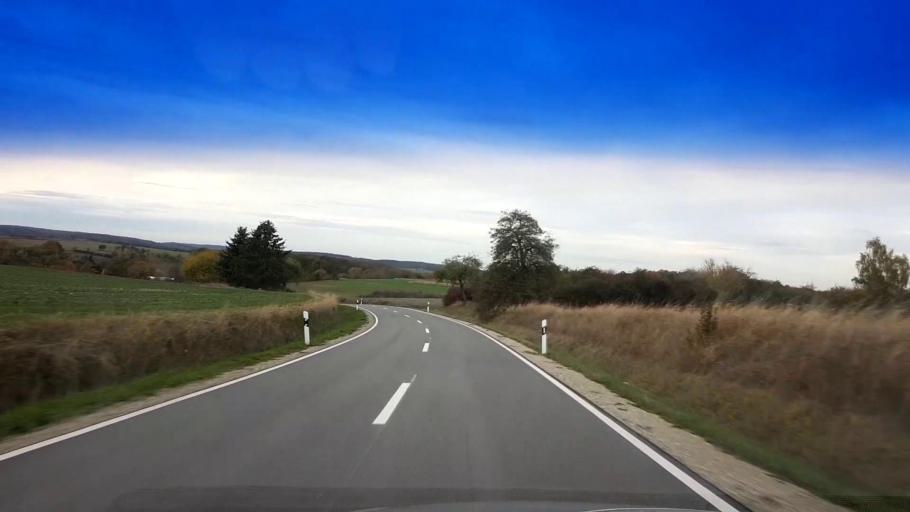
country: DE
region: Bavaria
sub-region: Upper Franconia
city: Priesendorf
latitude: 49.9287
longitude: 10.7030
